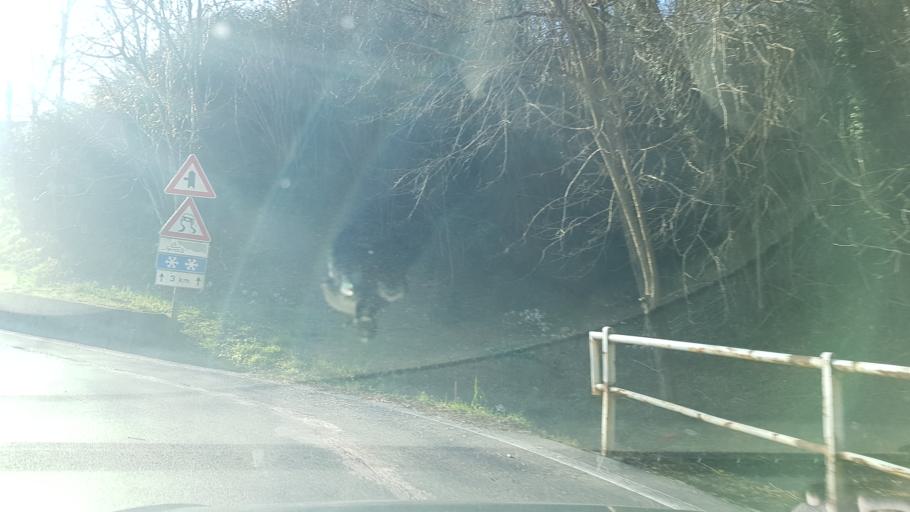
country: IT
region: Friuli Venezia Giulia
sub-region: Provincia di Udine
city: Forgaria nel Friuli
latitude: 46.2228
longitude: 12.9949
